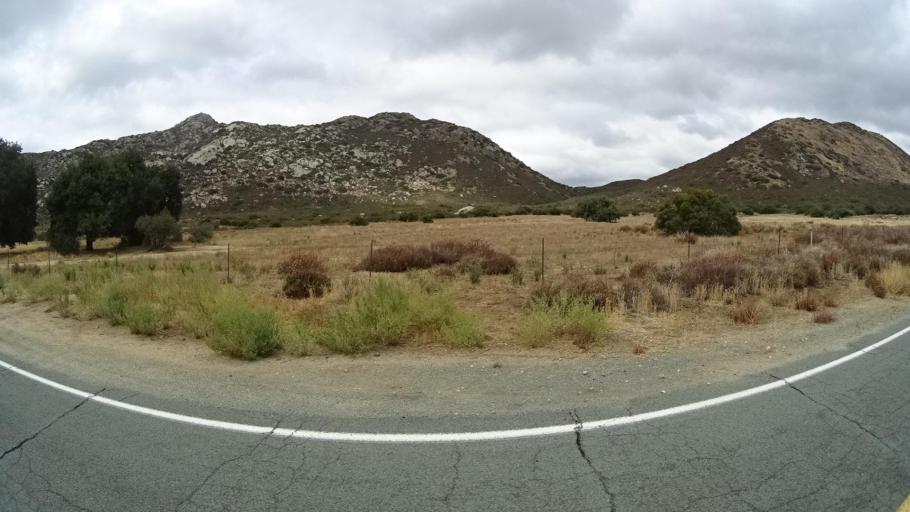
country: US
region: California
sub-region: San Diego County
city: Pine Valley
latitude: 32.7275
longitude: -116.4614
